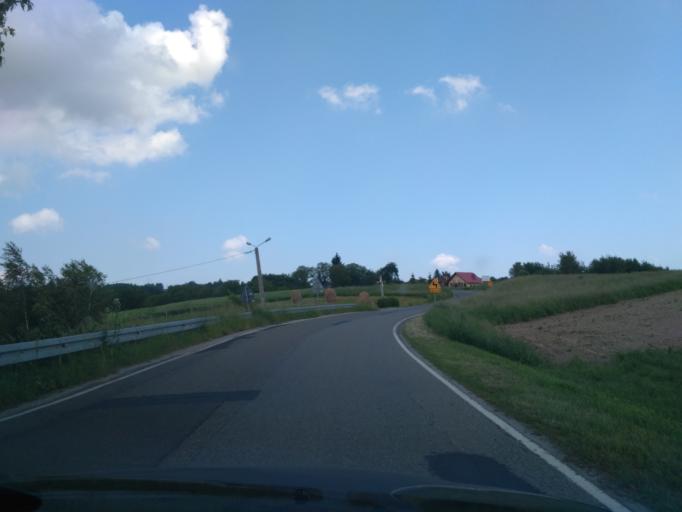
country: PL
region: Subcarpathian Voivodeship
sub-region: Powiat lancucki
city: Handzlowka
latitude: 49.9776
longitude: 22.1913
